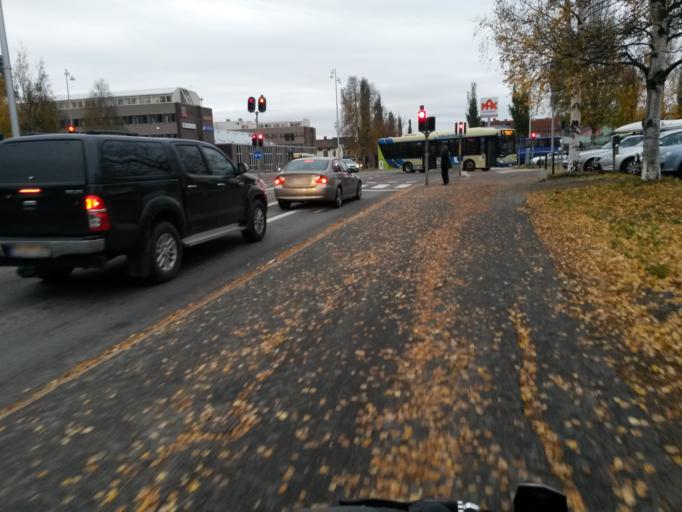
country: SE
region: Vaesterbotten
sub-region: Skelleftea Kommun
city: Skelleftea
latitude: 64.7517
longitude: 20.9608
